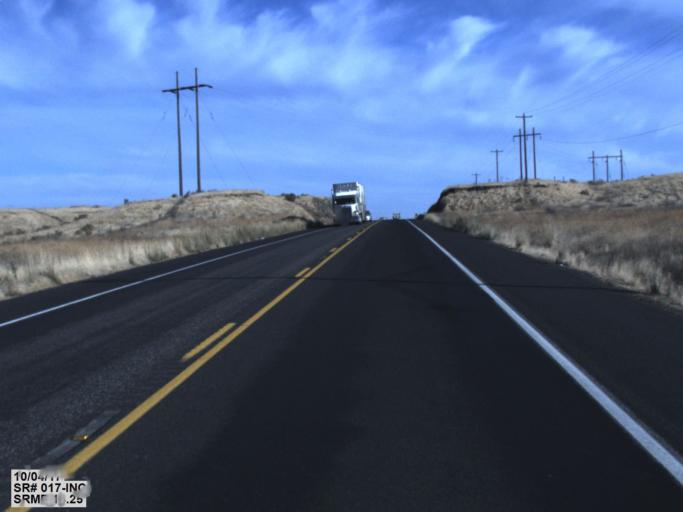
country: US
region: Washington
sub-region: Franklin County
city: Connell
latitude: 46.6587
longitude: -119.0064
